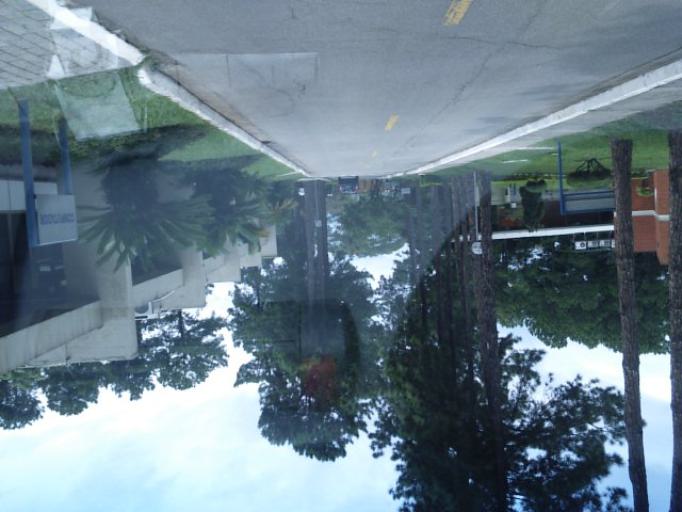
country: BR
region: Sao Paulo
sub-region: Sao Jose Dos Campos
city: Sao Jose dos Campos
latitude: -23.2095
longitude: -45.8602
